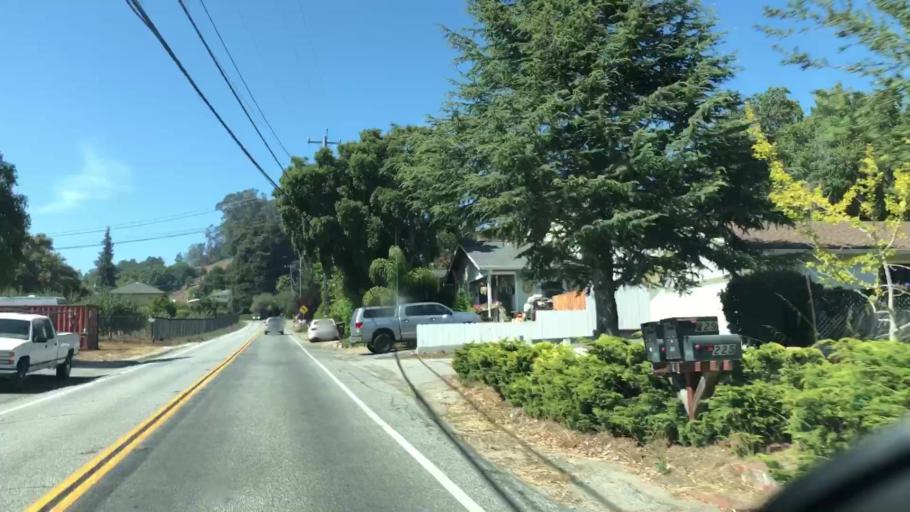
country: US
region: California
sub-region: Santa Cruz County
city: Corralitos
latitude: 36.9905
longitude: -121.8109
